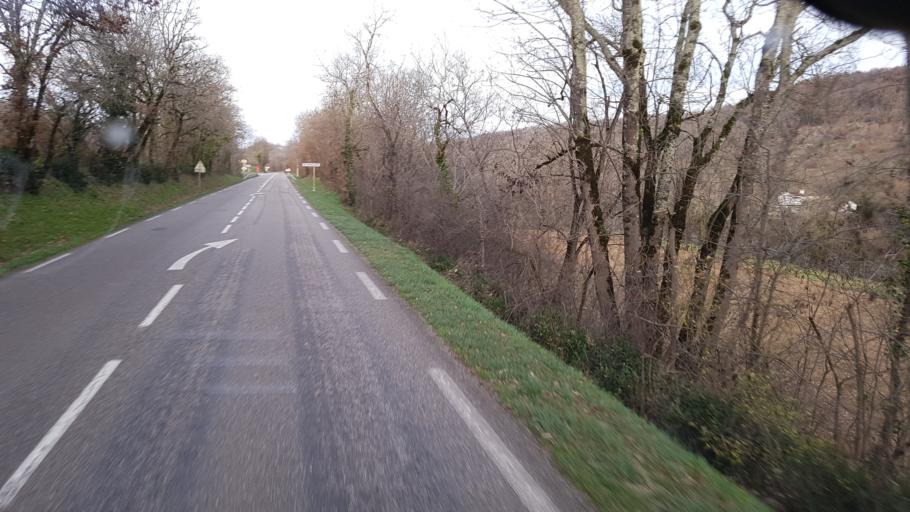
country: FR
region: Midi-Pyrenees
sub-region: Departement du Tarn-et-Garonne
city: Montricoux
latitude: 44.0691
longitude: 1.6517
